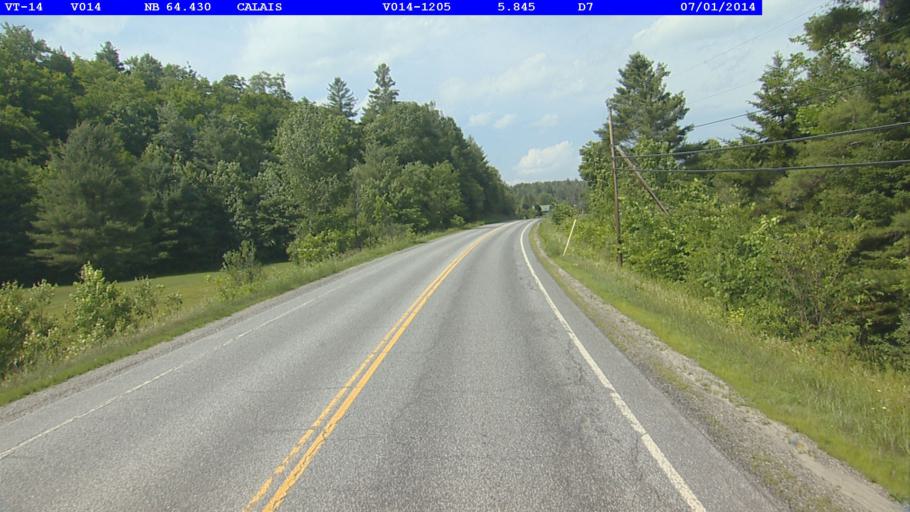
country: US
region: Vermont
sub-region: Caledonia County
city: Hardwick
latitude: 44.3815
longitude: -72.4185
